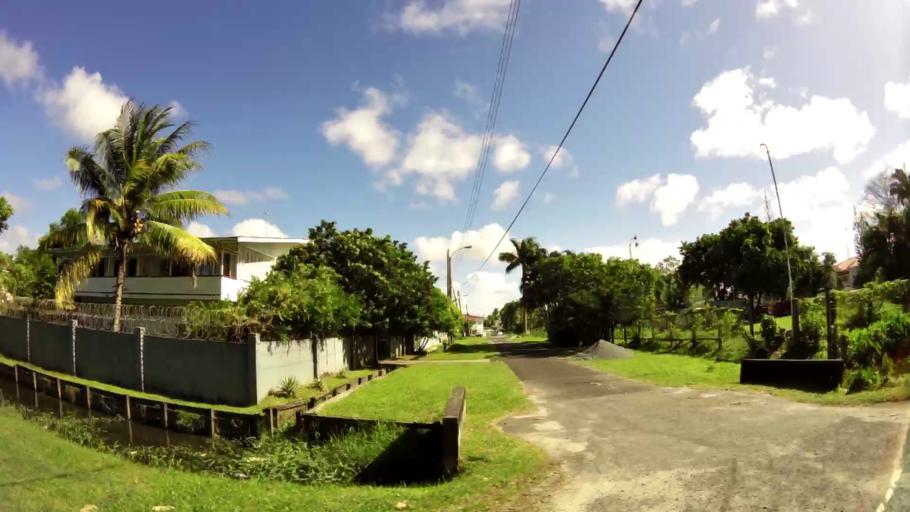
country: GY
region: Demerara-Mahaica
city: Georgetown
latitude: 6.8211
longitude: -58.1293
